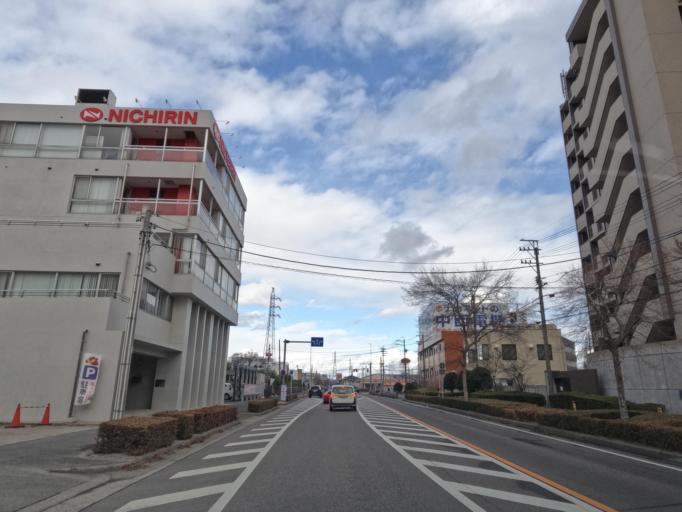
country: JP
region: Aichi
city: Chiryu
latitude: 34.9963
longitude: 137.0154
